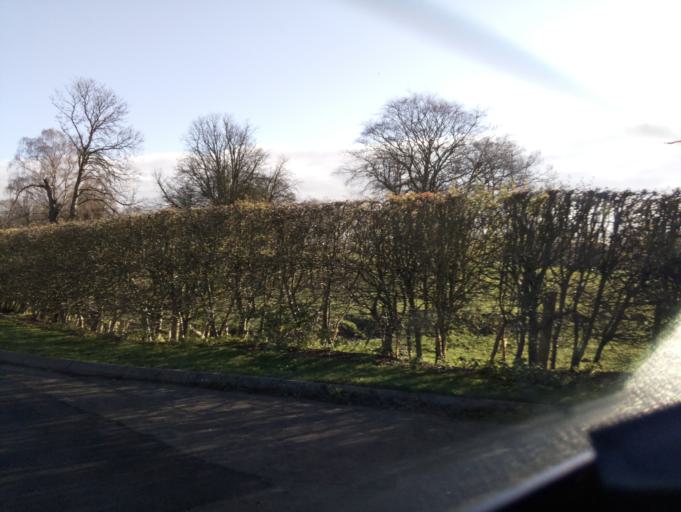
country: GB
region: England
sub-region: Staffordshire
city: Barton under Needwood
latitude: 52.8164
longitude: -1.7457
